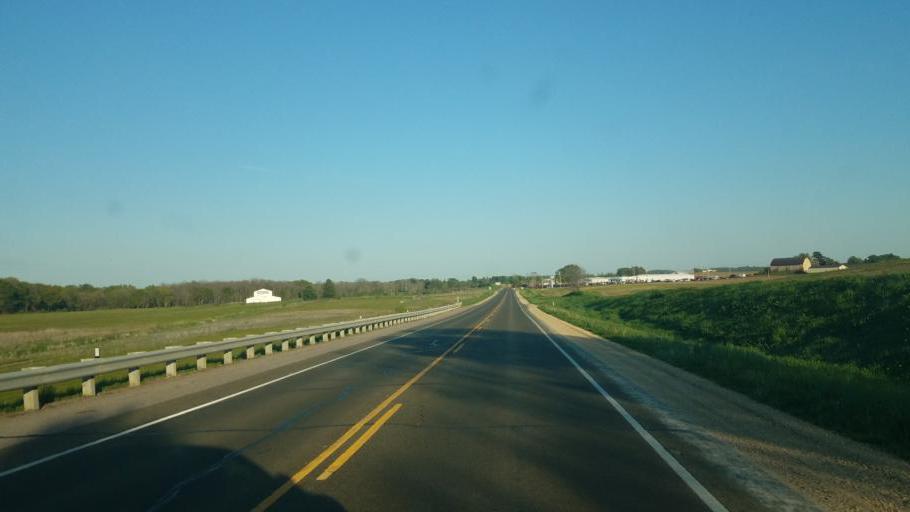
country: US
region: Wisconsin
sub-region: Sauk County
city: Reedsburg
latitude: 43.5502
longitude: -90.0582
